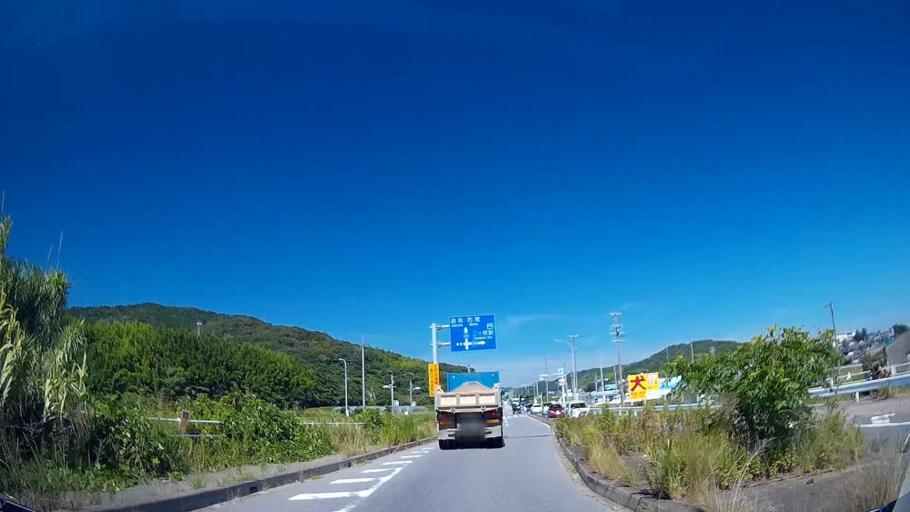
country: JP
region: Aichi
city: Gamagori
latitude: 34.8304
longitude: 137.1813
